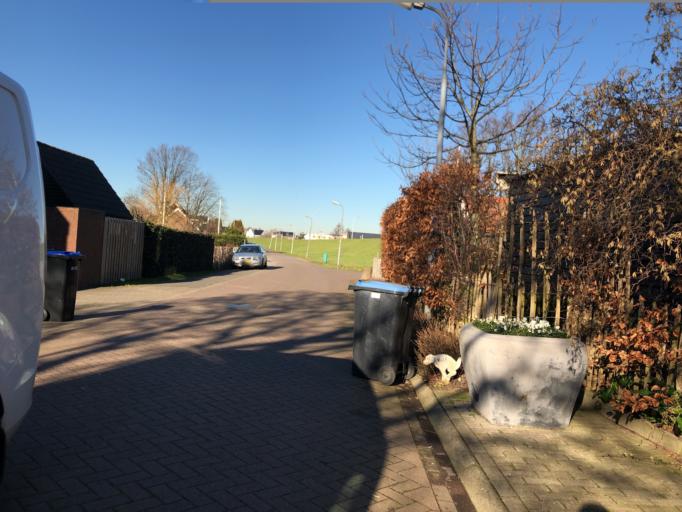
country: NL
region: North Holland
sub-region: Gemeente Zaanstad
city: Zaanstad
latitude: 52.4312
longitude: 4.7798
